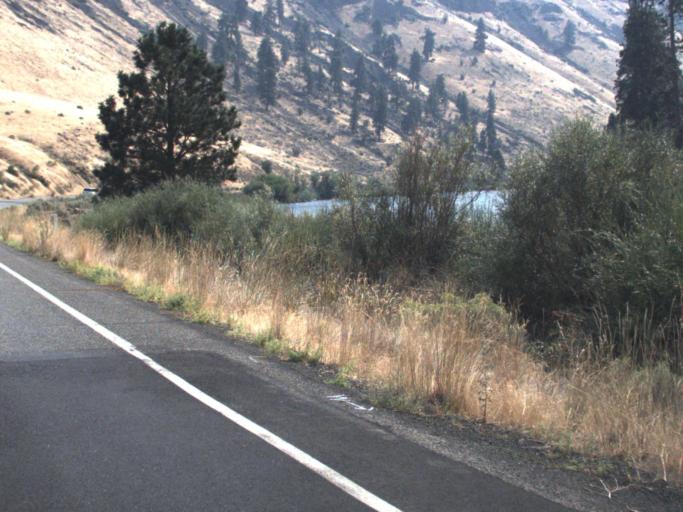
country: US
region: Washington
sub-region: Kittitas County
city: Kittitas
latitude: 46.8845
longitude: -120.4767
